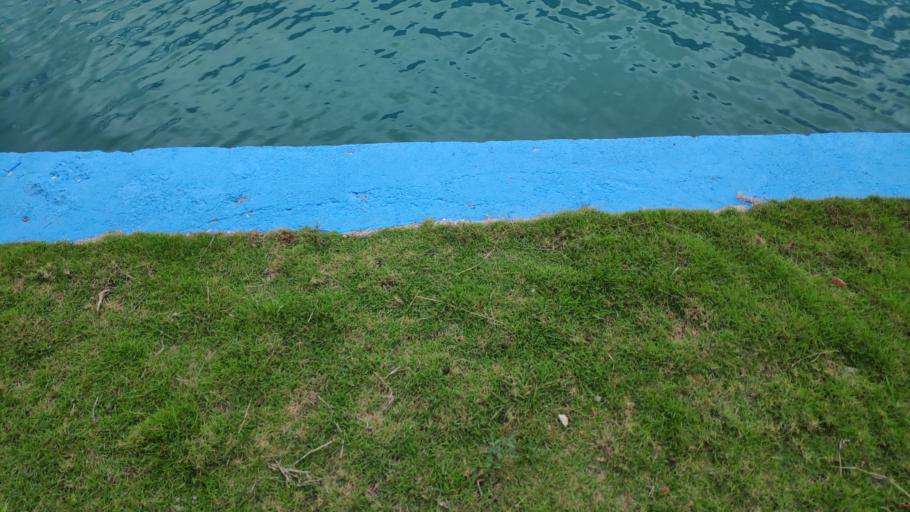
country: CU
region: Artemisa
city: Bauta
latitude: 23.0884
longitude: -82.4953
